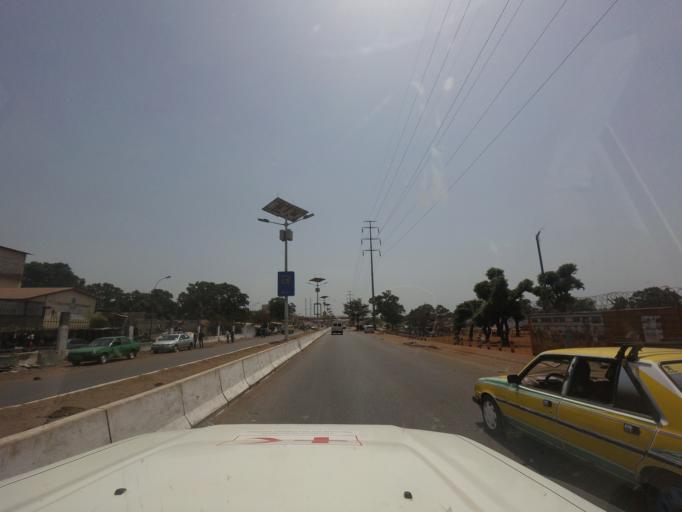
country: GN
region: Conakry
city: Conakry
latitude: 9.5508
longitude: -13.6597
